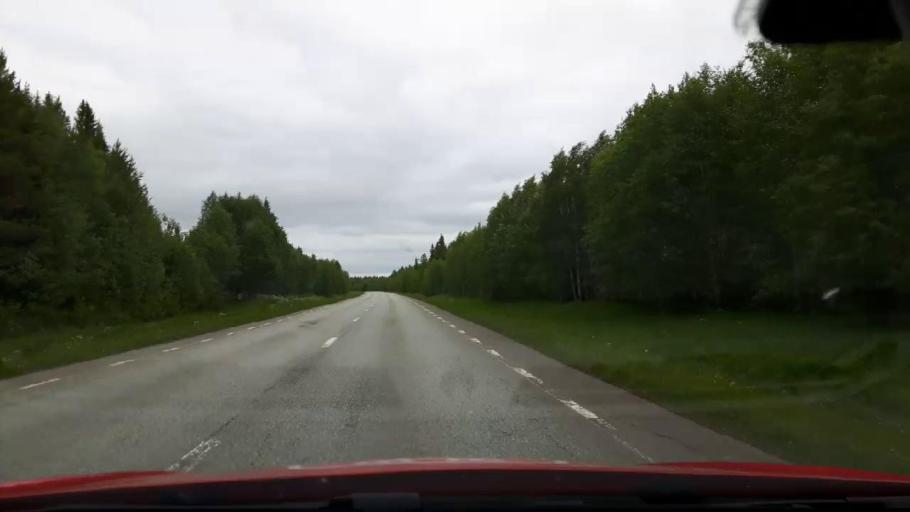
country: SE
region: Jaemtland
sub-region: OEstersunds Kommun
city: Lit
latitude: 63.5985
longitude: 14.6567
